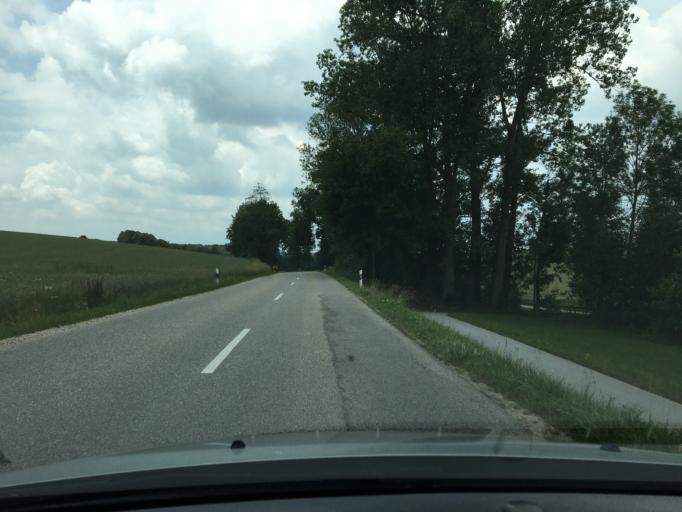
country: DE
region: Bavaria
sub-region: Lower Bavaria
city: Velden
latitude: 48.3864
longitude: 12.2988
